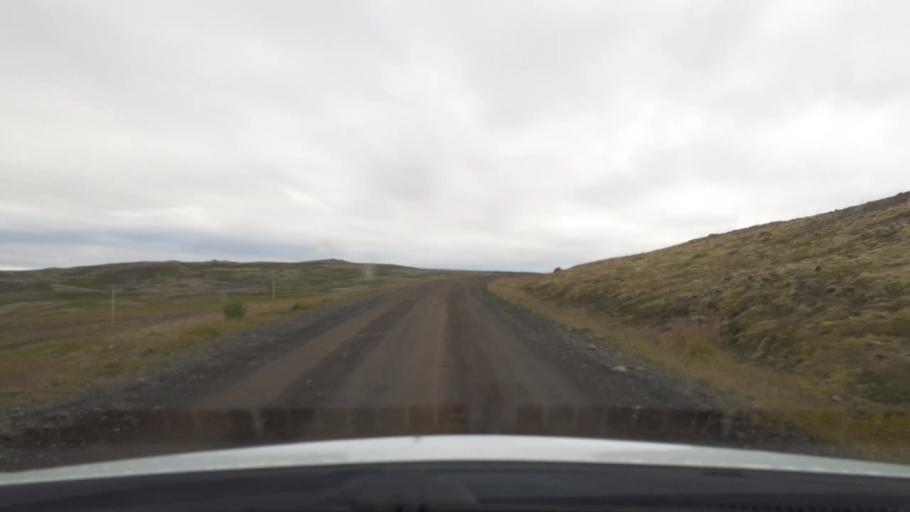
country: IS
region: Capital Region
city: Mosfellsbaer
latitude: 64.2065
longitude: -21.5649
